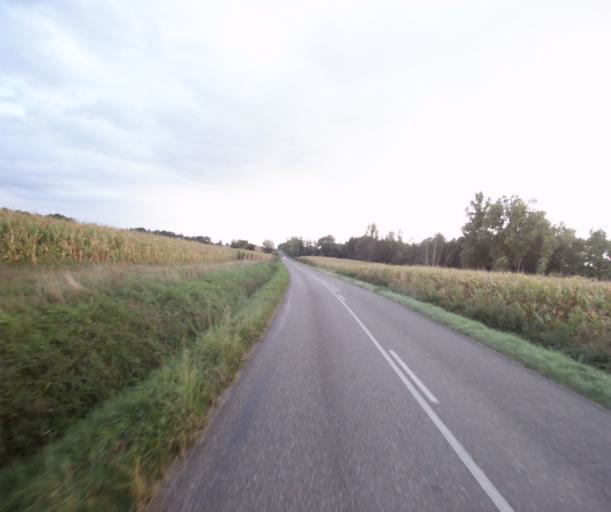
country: FR
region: Midi-Pyrenees
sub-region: Departement du Gers
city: Cazaubon
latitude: 43.9164
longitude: -0.0797
